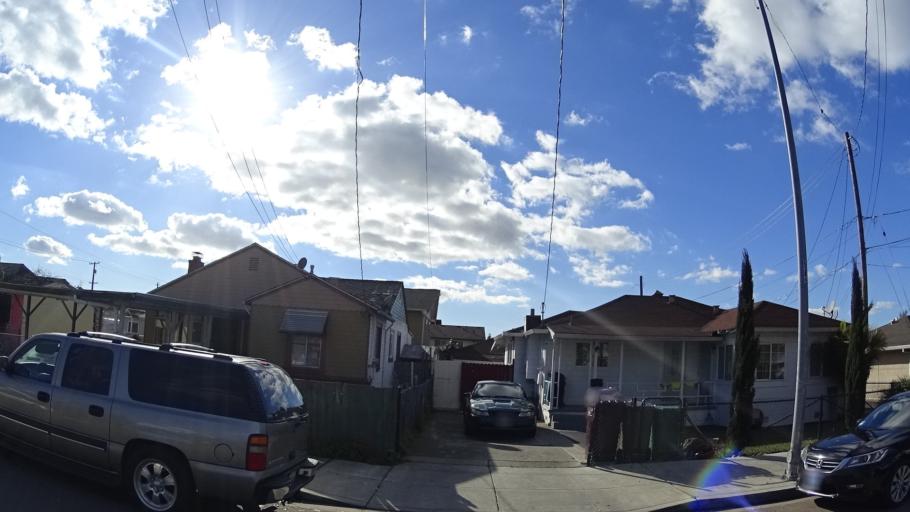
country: US
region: California
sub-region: Alameda County
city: Cherryland
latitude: 37.6739
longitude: -122.1004
